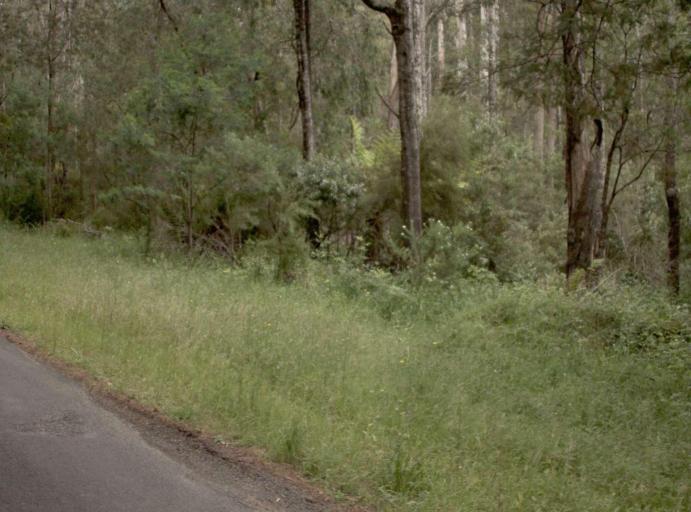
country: AU
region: Victoria
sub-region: Baw Baw
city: Warragul
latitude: -37.8904
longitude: 146.0905
